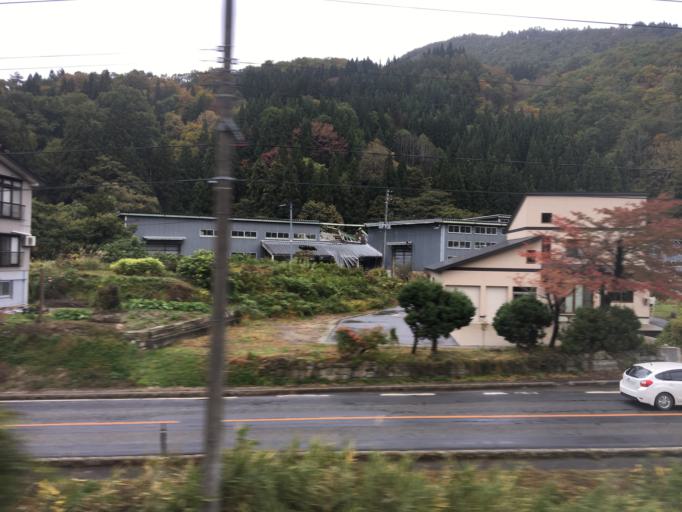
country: JP
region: Yamagata
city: Nagai
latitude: 38.0212
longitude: 139.8828
